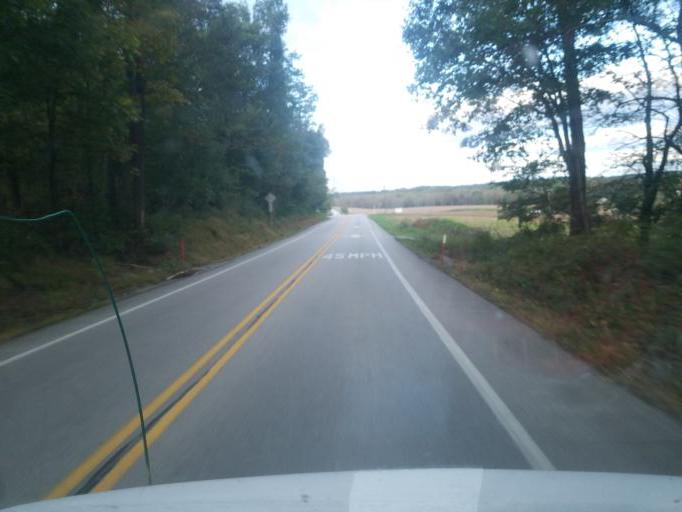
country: US
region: Pennsylvania
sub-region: York County
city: Weigelstown
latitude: 39.9412
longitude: -76.8584
